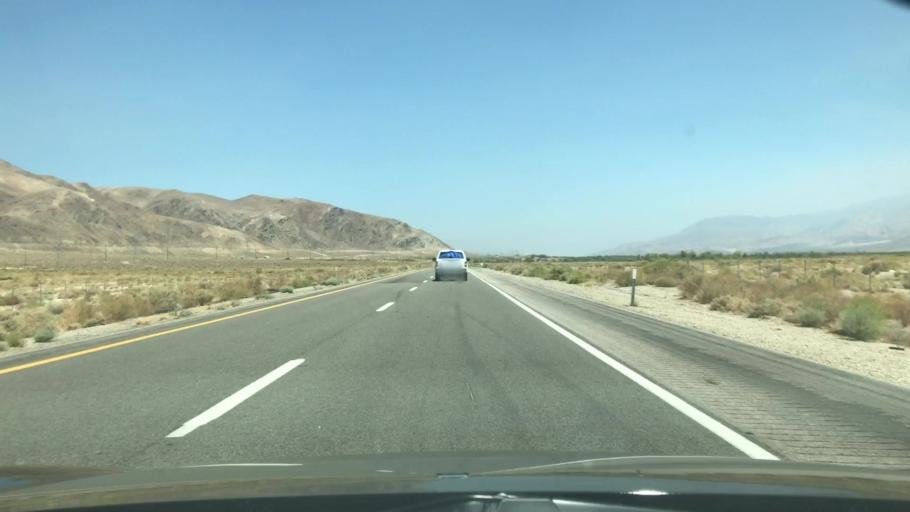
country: US
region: California
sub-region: Inyo County
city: Lone Pine
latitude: 36.6486
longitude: -118.0858
